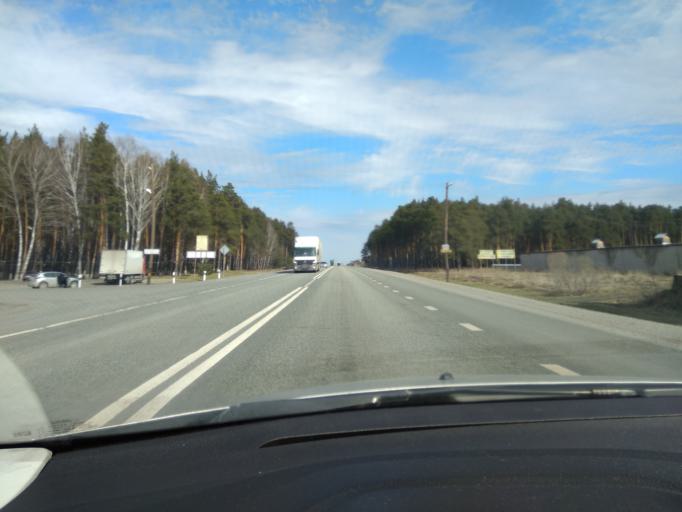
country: RU
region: Sverdlovsk
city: Troitskiy
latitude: 57.0874
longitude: 63.7450
